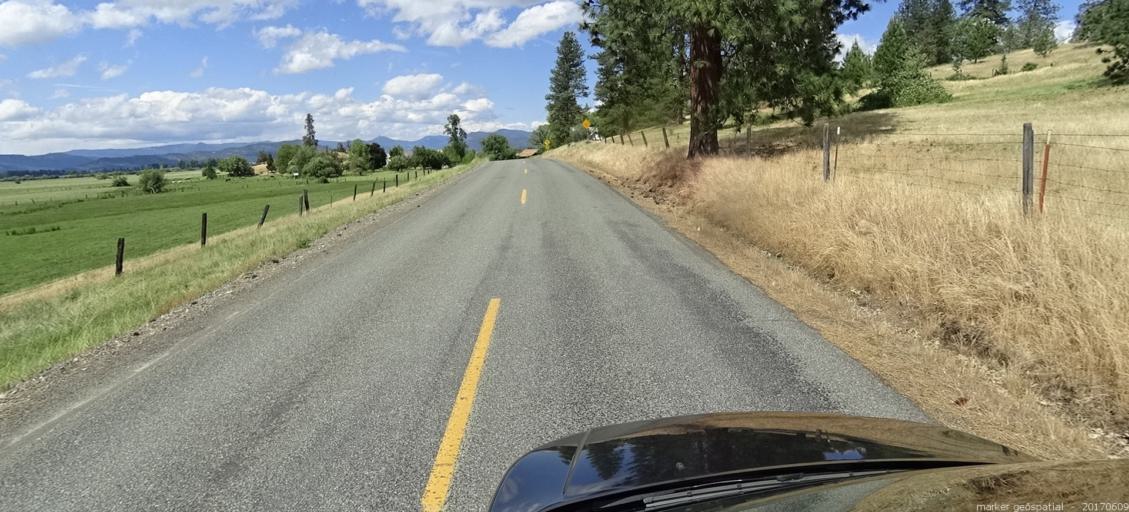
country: US
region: California
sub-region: Siskiyou County
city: Yreka
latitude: 41.4782
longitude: -122.8778
